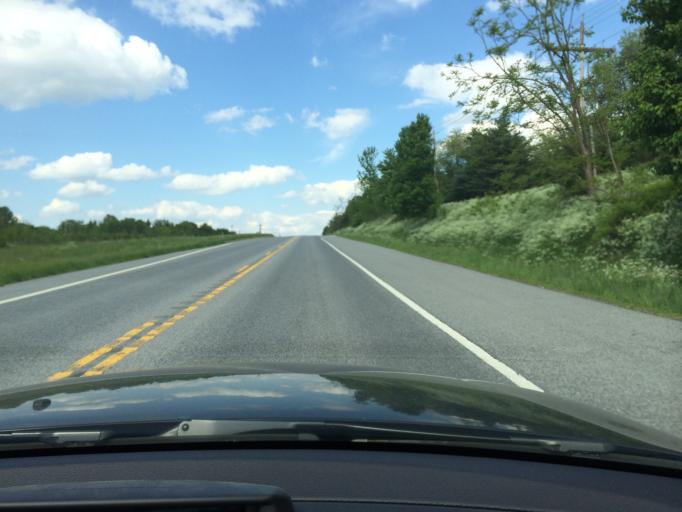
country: US
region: Maryland
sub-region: Carroll County
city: Westminster
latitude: 39.5629
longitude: -77.0263
